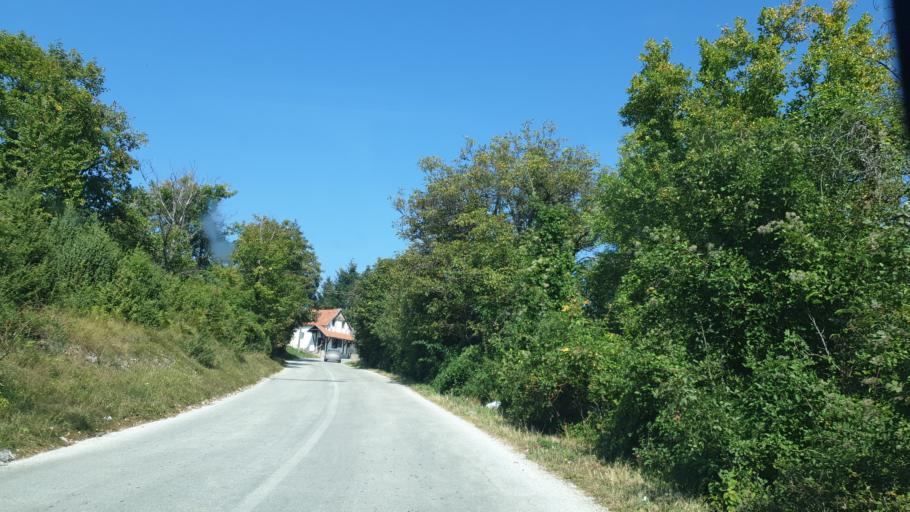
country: RS
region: Central Serbia
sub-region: Zlatiborski Okrug
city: Cajetina
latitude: 43.7195
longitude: 19.8337
